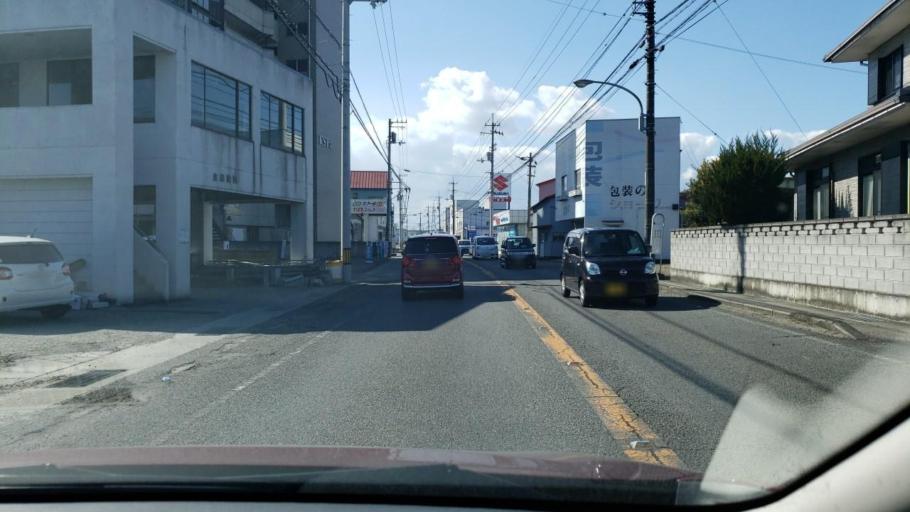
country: JP
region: Tokushima
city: Ishii
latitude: 34.1353
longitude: 134.4947
